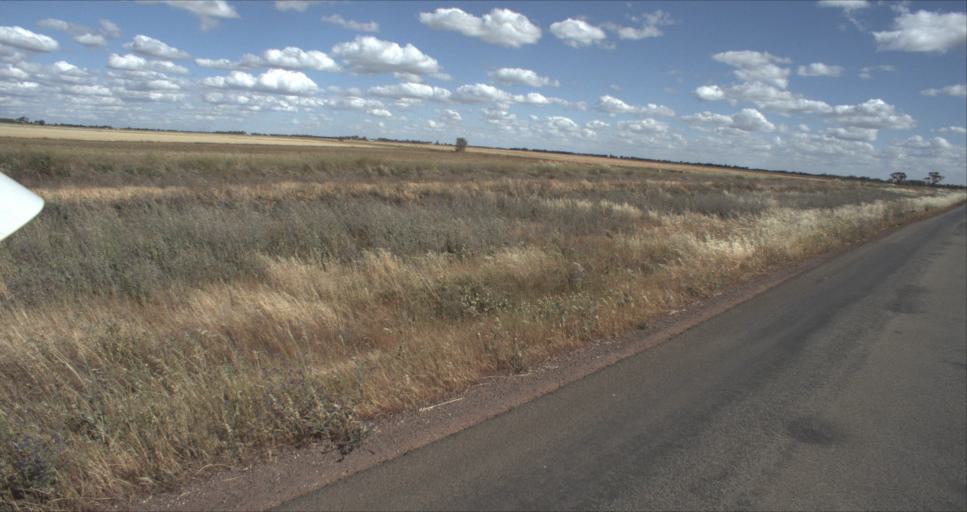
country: AU
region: New South Wales
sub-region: Leeton
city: Leeton
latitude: -34.4223
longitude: 146.2639
